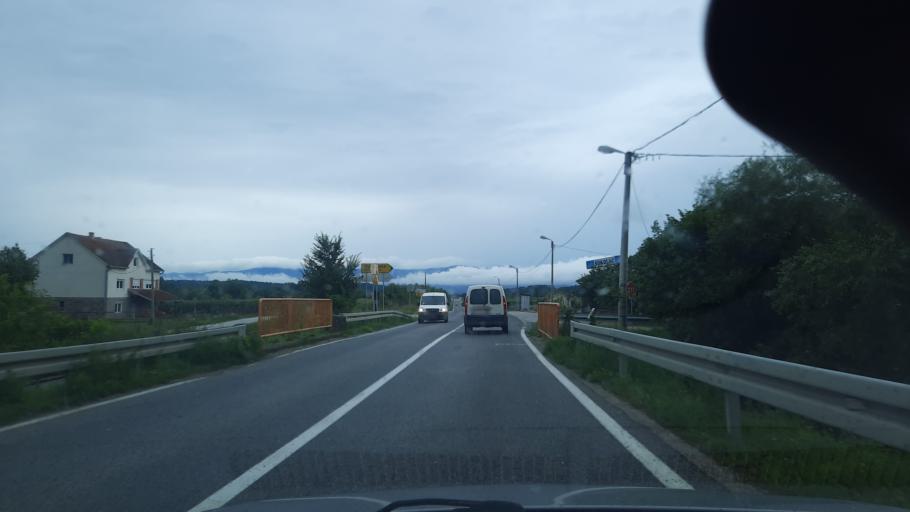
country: RS
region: Central Serbia
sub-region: Raski Okrug
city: Kraljevo
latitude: 43.7605
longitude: 20.8054
